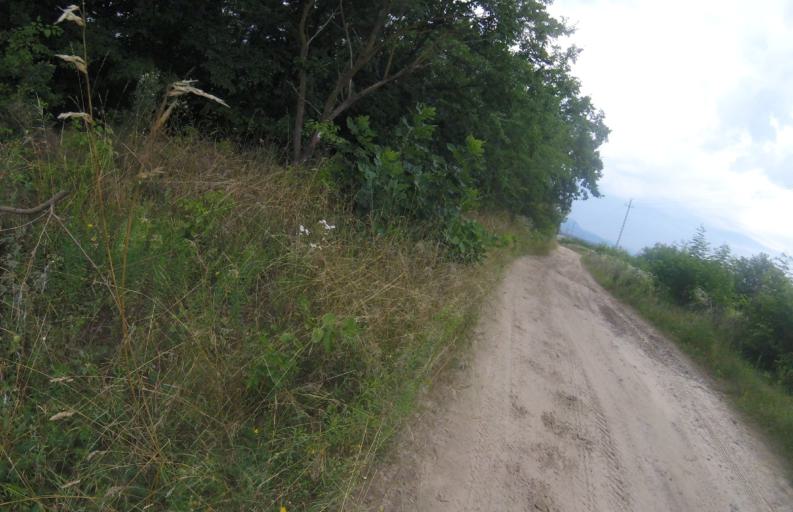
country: HU
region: Pest
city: God
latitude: 47.6652
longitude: 19.1698
